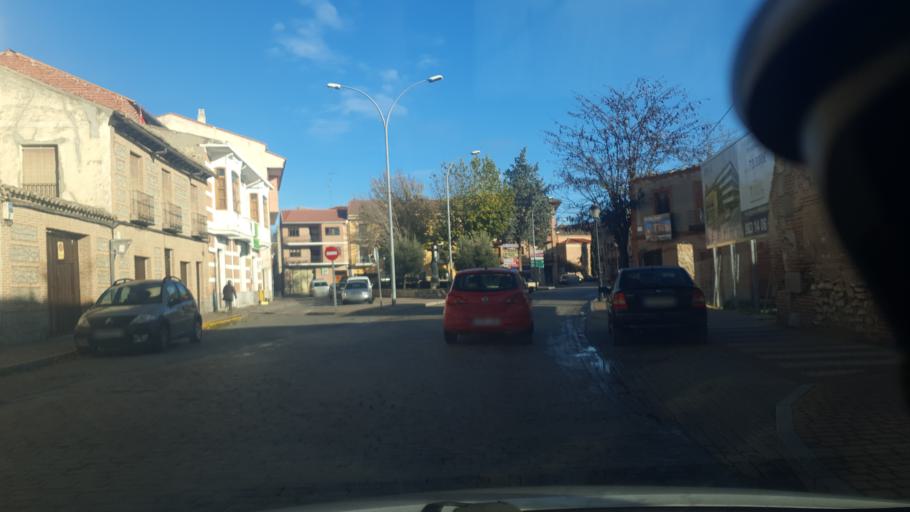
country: ES
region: Castille and Leon
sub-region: Provincia de Avila
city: Arevalo
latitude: 41.0604
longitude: -4.7205
